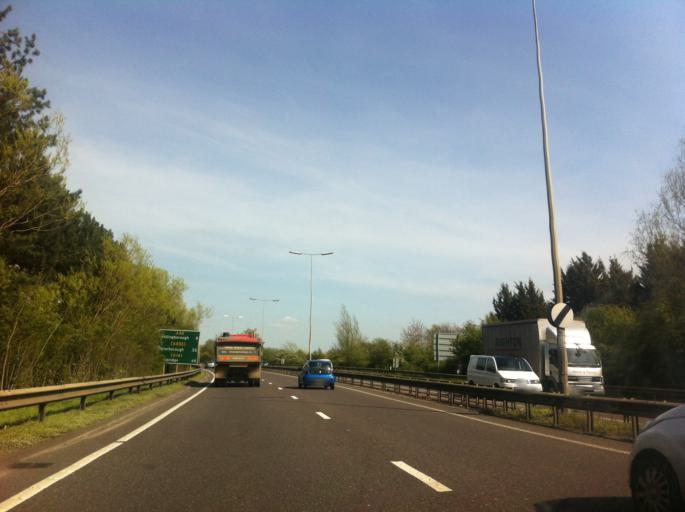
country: GB
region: England
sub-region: Northamptonshire
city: Northampton
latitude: 52.2467
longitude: -0.8251
